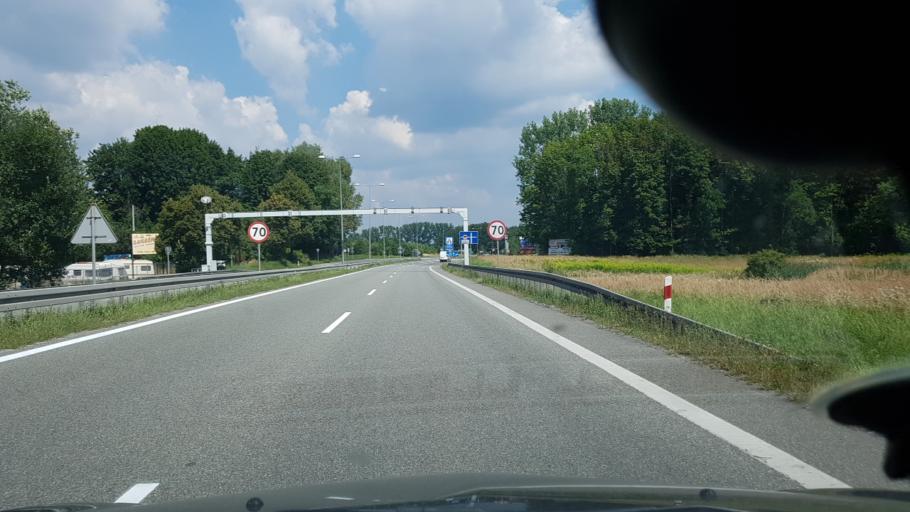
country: PL
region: Silesian Voivodeship
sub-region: Powiat mikolowski
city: Laziska Gorne
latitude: 50.1656
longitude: 18.8515
